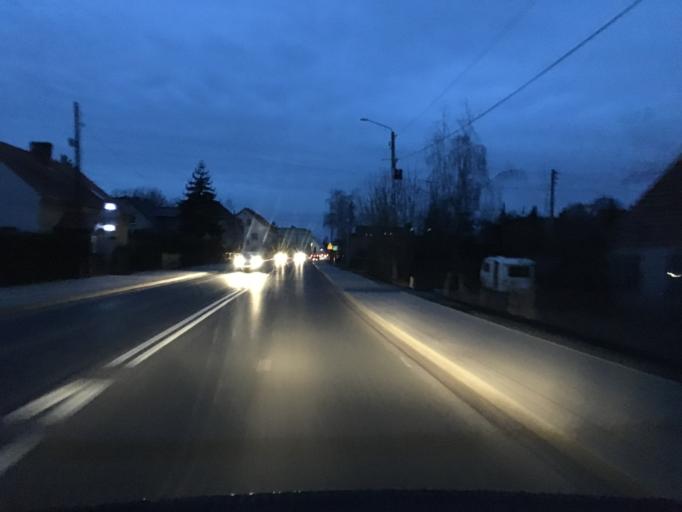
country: PL
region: Opole Voivodeship
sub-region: Powiat brzeski
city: Losiow
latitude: 50.7905
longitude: 17.5661
